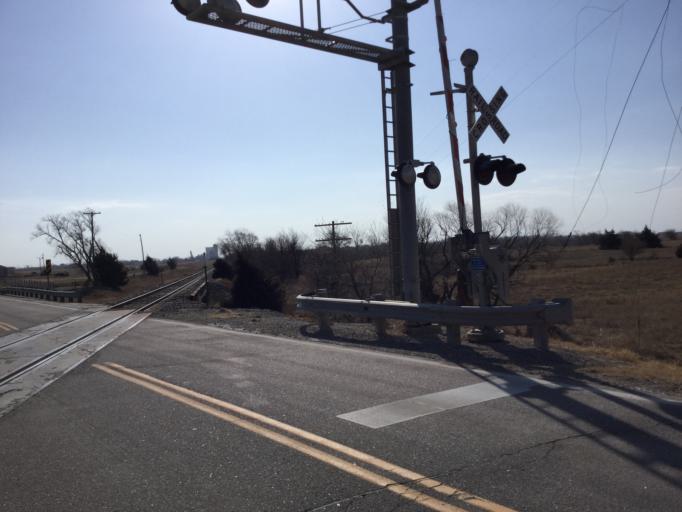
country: US
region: Kansas
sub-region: Rush County
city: La Crosse
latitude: 38.5391
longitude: -99.3269
